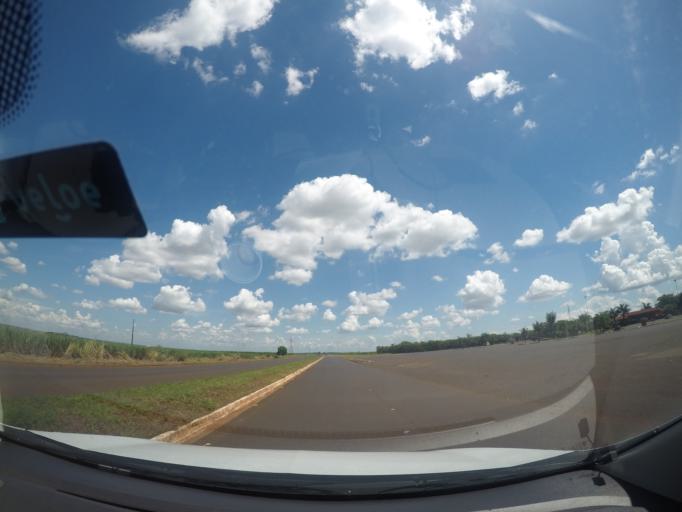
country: BR
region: Minas Gerais
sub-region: Frutal
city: Frutal
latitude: -19.8155
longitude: -48.7307
